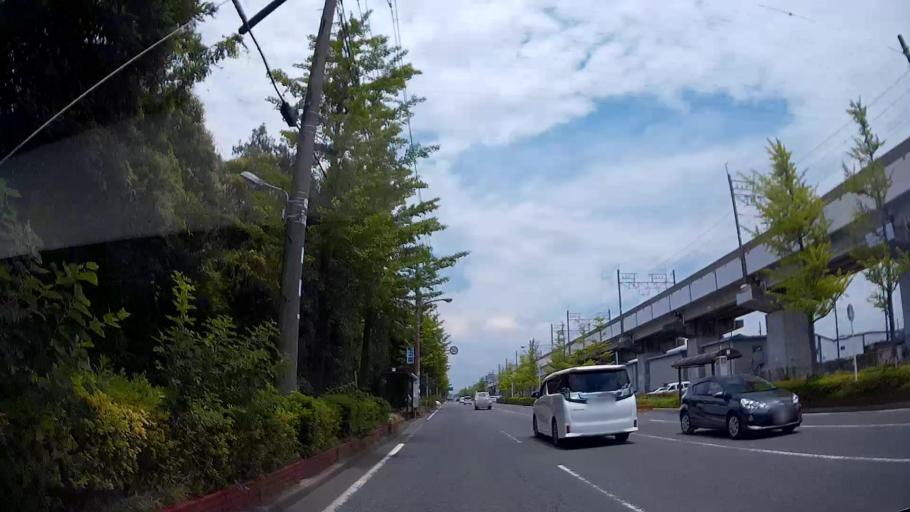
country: JP
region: Tokyo
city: Urayasu
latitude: 35.6383
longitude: 139.8985
